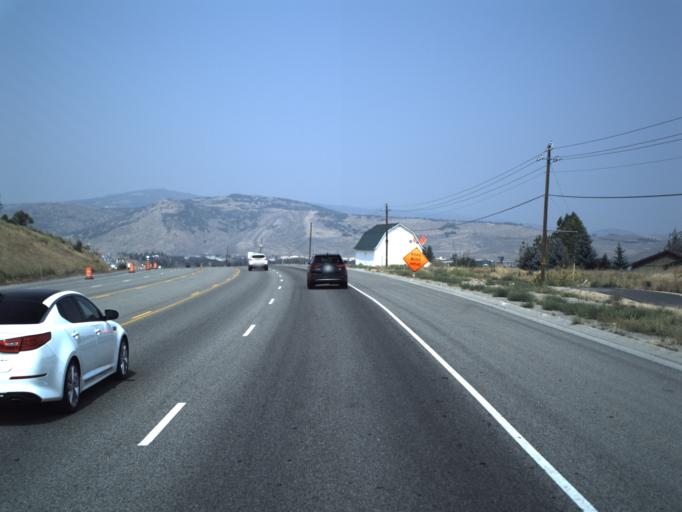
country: US
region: Utah
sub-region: Summit County
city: Snyderville
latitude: 40.7107
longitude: -111.5451
